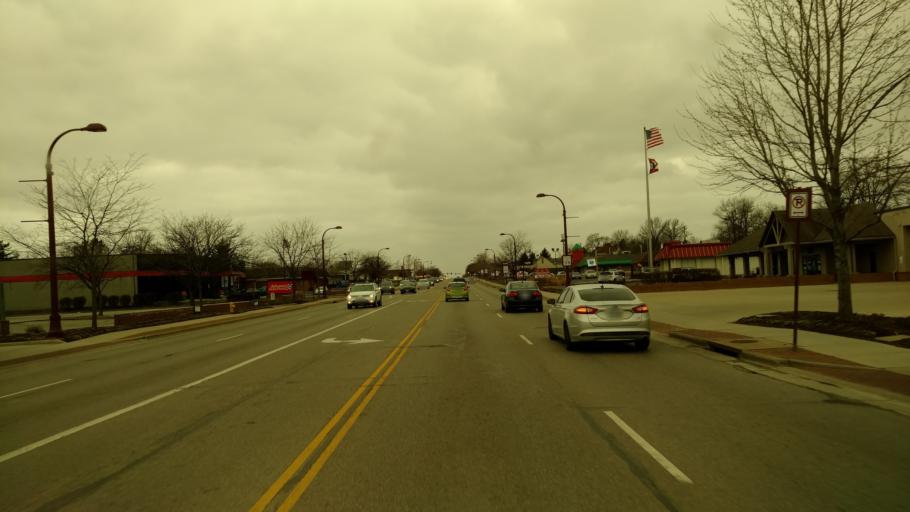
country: US
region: Ohio
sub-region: Franklin County
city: Reynoldsburg
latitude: 39.9552
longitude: -82.8124
